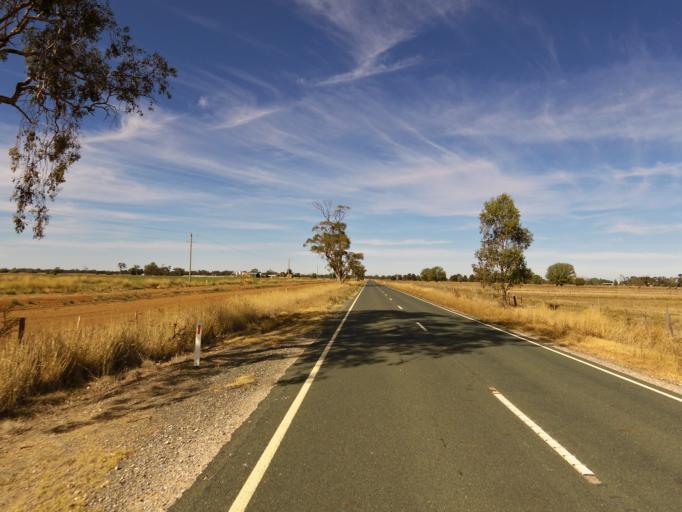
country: AU
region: Victoria
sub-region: Campaspe
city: Echuca
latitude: -36.2901
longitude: 144.5358
